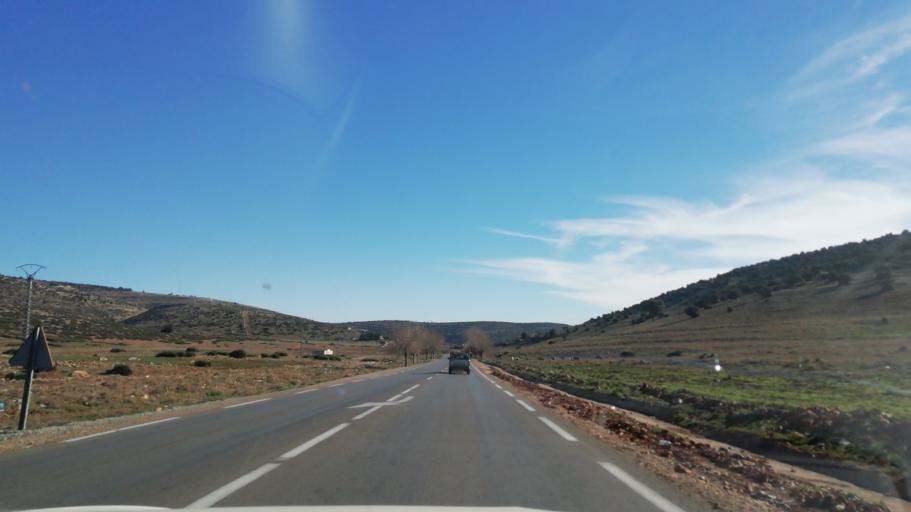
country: DZ
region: Tlemcen
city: Sebdou
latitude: 34.7134
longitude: -1.3252
